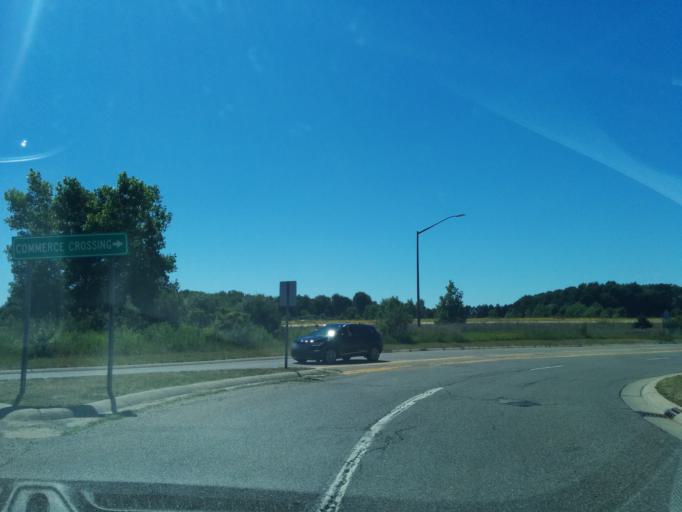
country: US
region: Michigan
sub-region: Oakland County
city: Walled Lake
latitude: 42.5357
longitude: -83.4481
